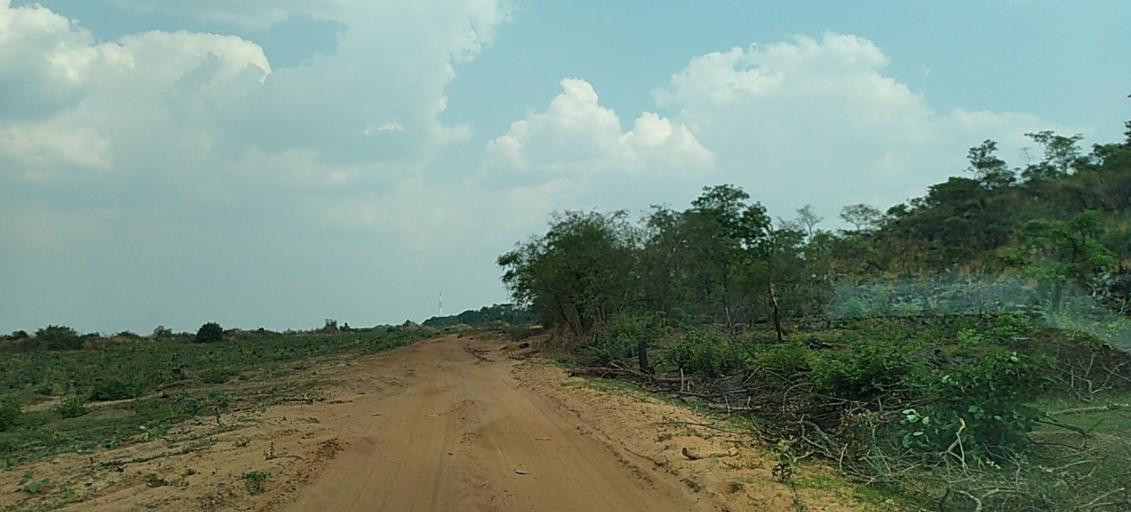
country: ZM
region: Copperbelt
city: Chingola
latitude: -12.7427
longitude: 27.7767
